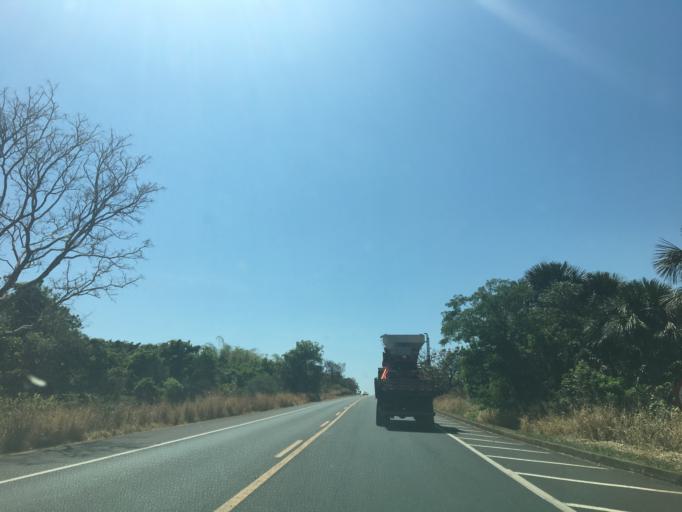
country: BR
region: Minas Gerais
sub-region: Monte Alegre De Minas
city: Monte Alegre de Minas
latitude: -18.9035
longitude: -49.0411
